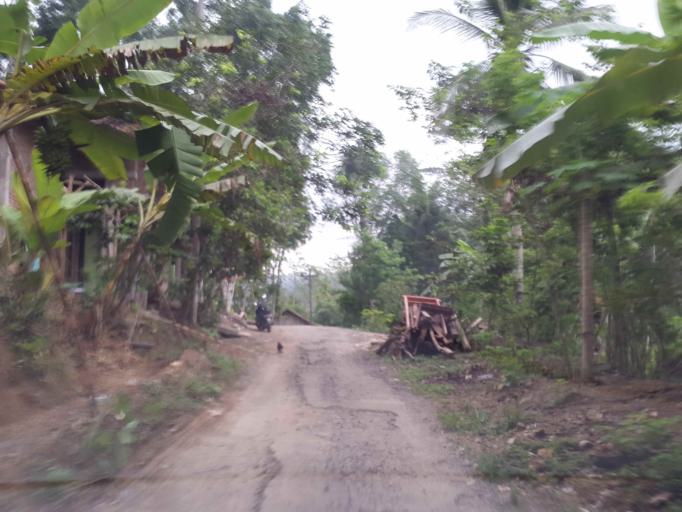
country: ID
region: Central Java
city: Genteng Wetan
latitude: -7.3566
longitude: 108.8927
